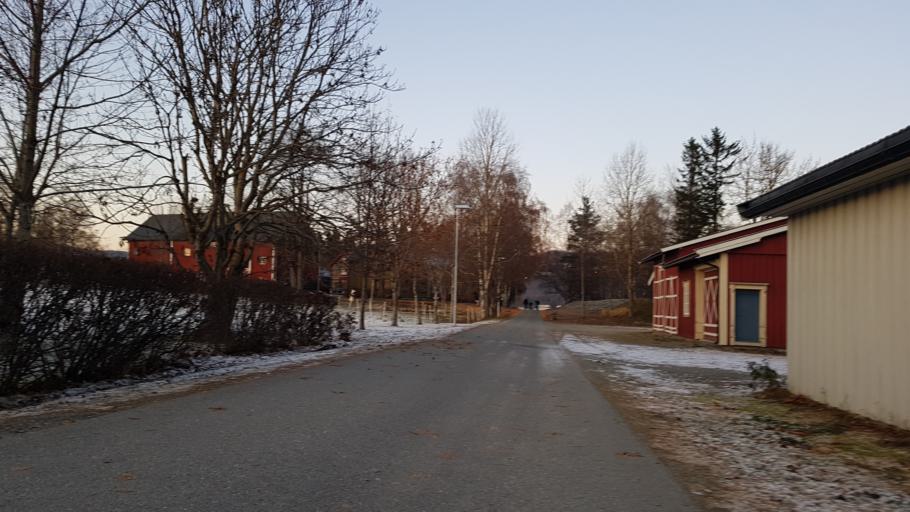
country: NO
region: Sor-Trondelag
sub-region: Melhus
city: Melhus
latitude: 63.2765
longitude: 10.2913
